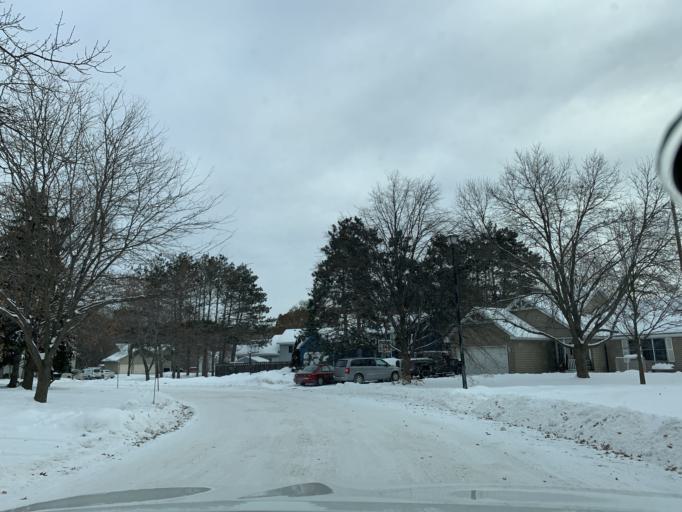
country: US
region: Minnesota
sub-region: Hennepin County
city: West Coon Rapids
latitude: 45.1681
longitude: -93.3020
